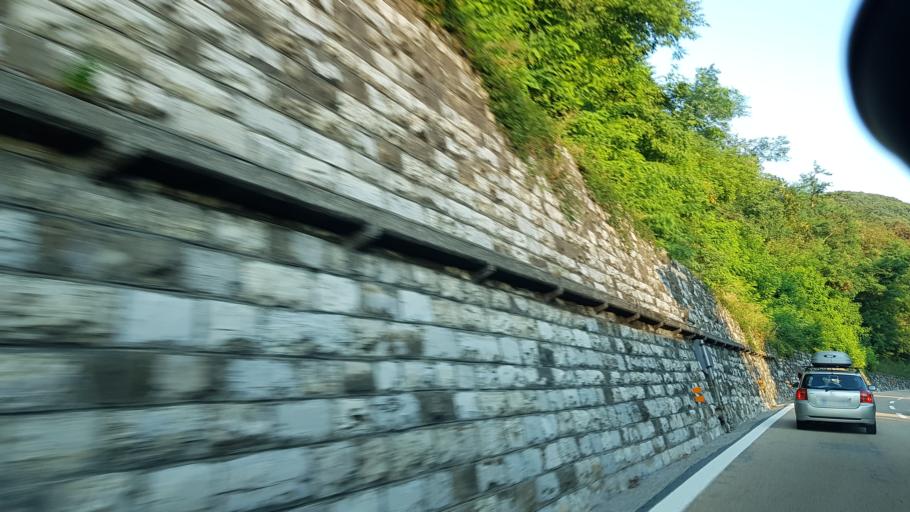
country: IT
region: Liguria
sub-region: Provincia di Genova
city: Busalla
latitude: 44.5639
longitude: 8.9457
